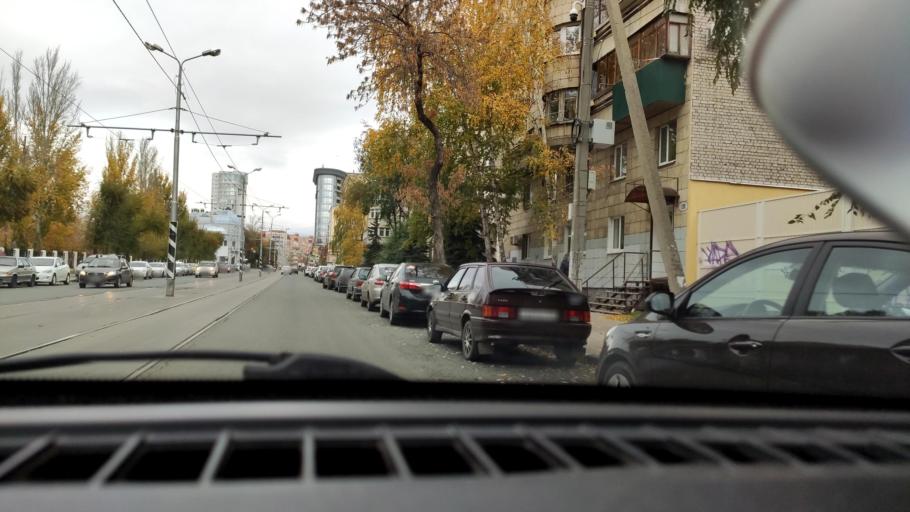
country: RU
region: Samara
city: Samara
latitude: 53.1952
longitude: 50.1045
